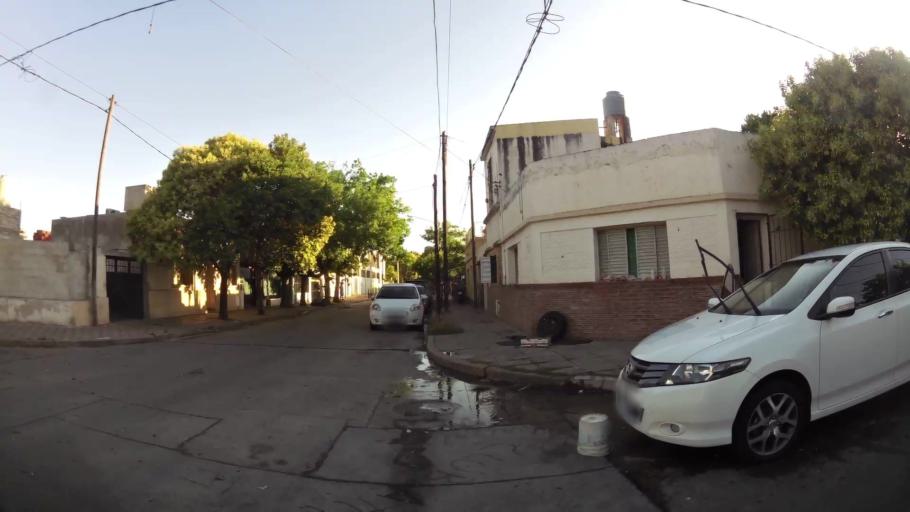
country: AR
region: Cordoba
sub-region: Departamento de Capital
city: Cordoba
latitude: -31.3734
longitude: -64.2098
